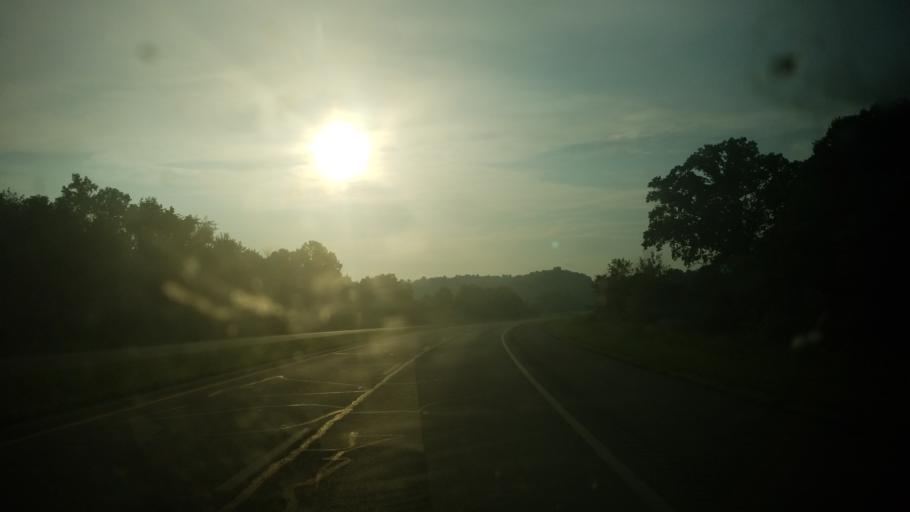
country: US
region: Ohio
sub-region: Pike County
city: Piketon
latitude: 39.0482
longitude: -83.0543
